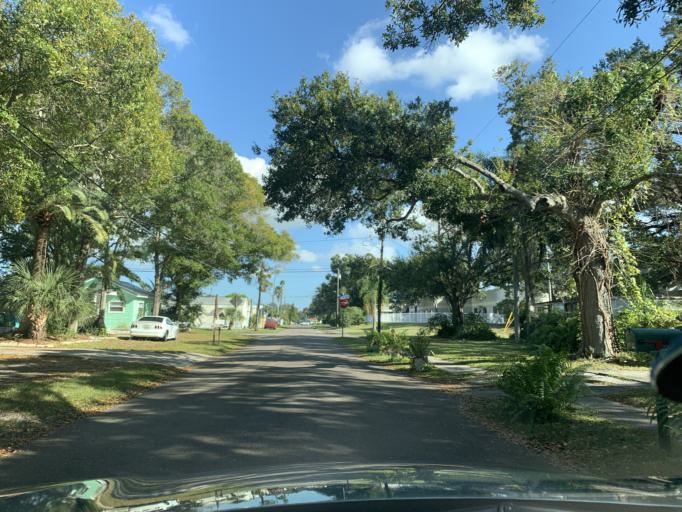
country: US
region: Florida
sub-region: Pinellas County
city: Belleair
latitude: 27.9259
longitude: -82.7989
